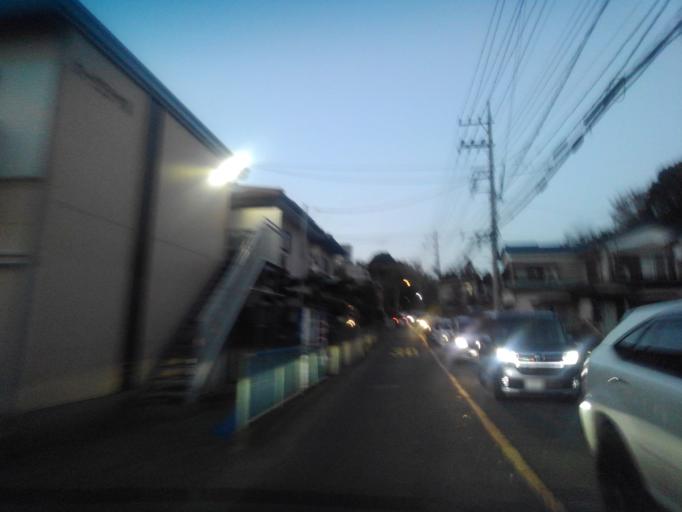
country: JP
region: Kanagawa
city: Minami-rinkan
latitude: 35.5013
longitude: 139.4644
